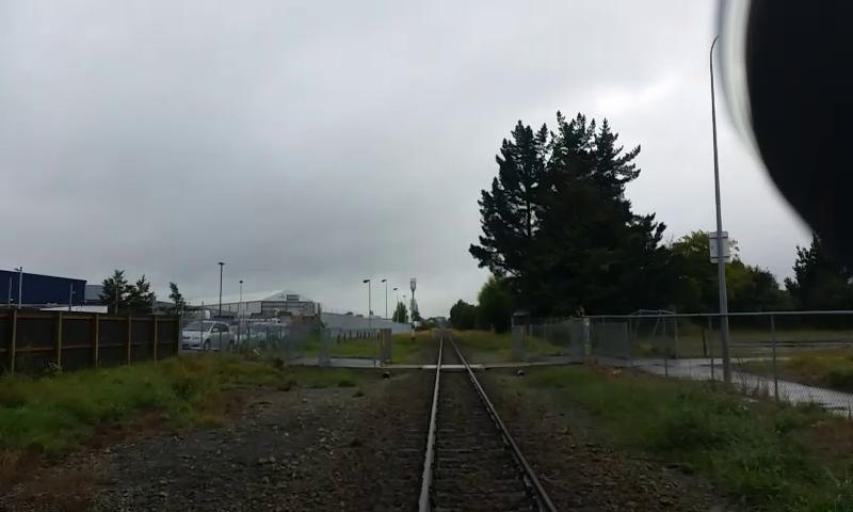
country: NZ
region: Canterbury
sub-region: Christchurch City
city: Christchurch
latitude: -43.5361
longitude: 172.6097
